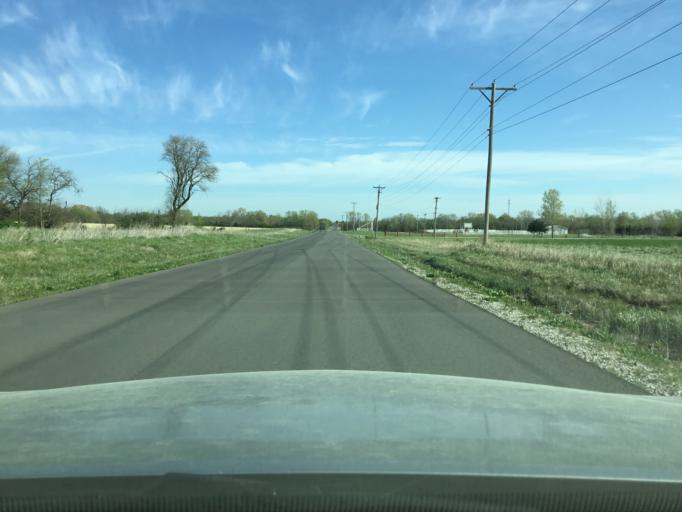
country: US
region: Kansas
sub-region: Neosho County
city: Chanute
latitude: 37.6521
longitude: -95.4435
